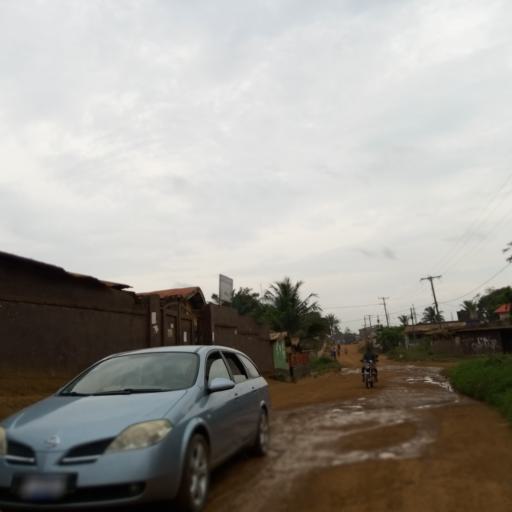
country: LR
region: Montserrado
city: Monrovia
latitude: 6.2953
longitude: -10.6795
